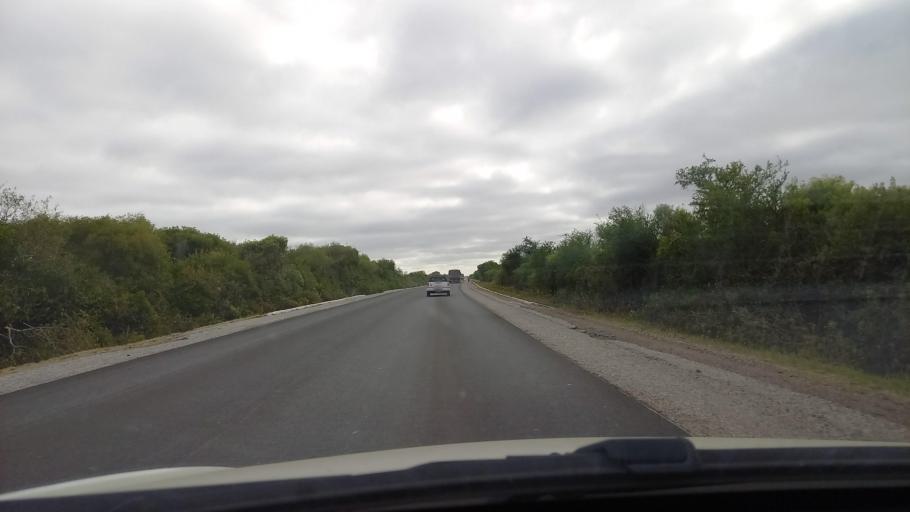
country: BR
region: Rio Grande do Sul
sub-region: Dom Pedrito
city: Dom Pedrito
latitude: -30.9554
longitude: -54.6932
